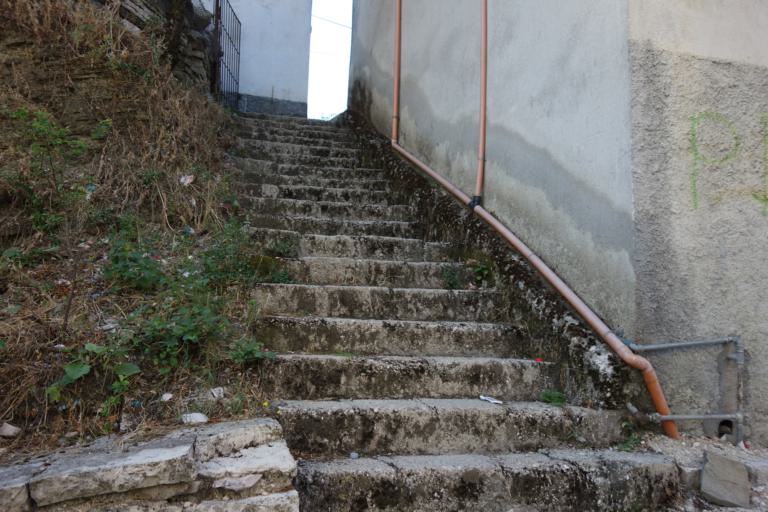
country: AL
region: Gjirokaster
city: Gjirokaster
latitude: 40.0806
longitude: 20.1446
